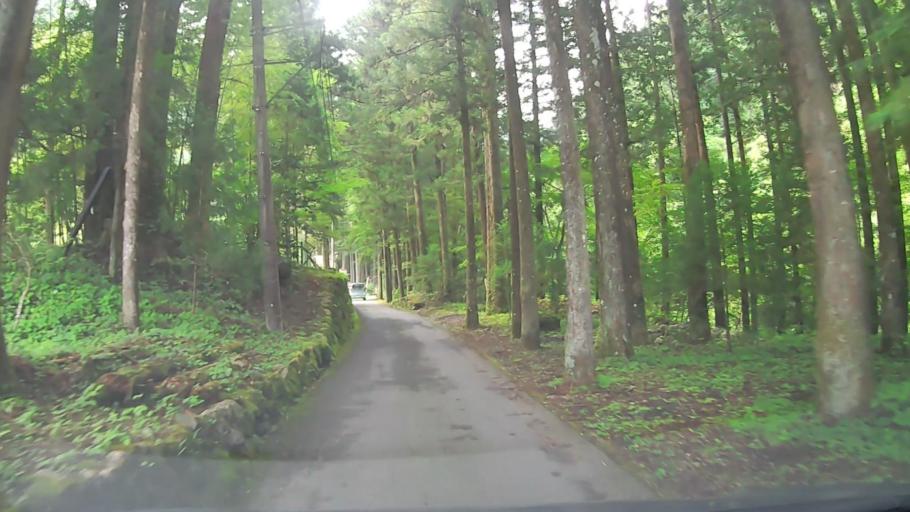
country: JP
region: Tokyo
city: Itsukaichi
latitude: 35.7502
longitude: 139.1164
